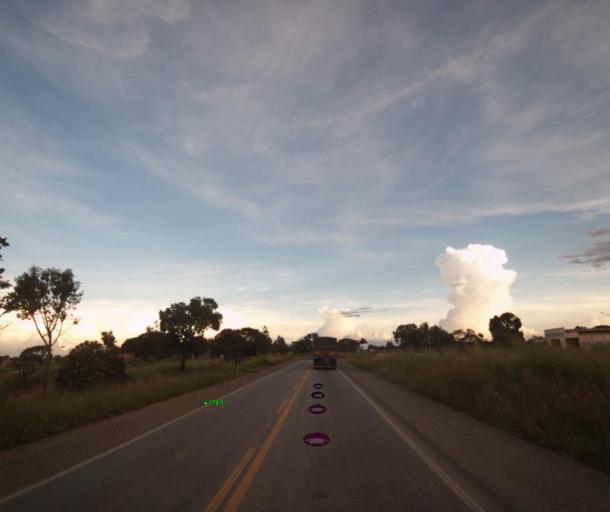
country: BR
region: Goias
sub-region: Uruacu
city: Uruacu
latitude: -14.3003
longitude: -49.1485
